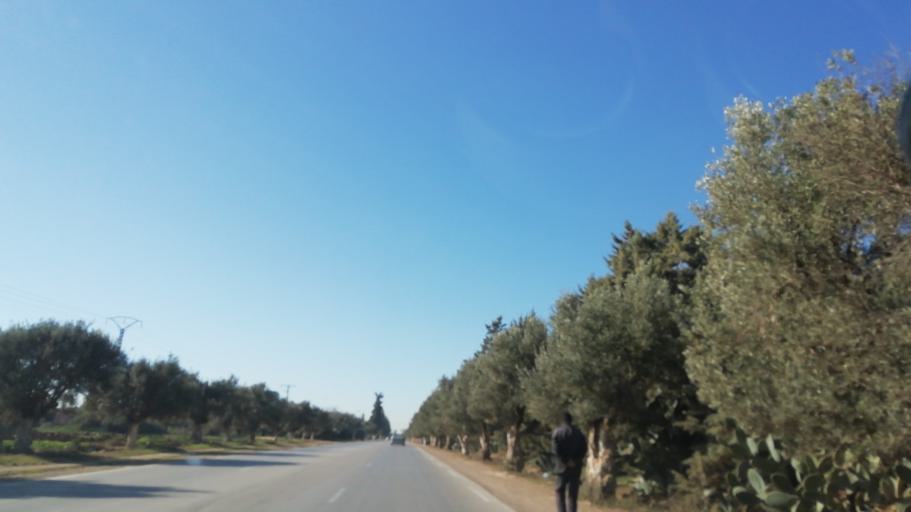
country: DZ
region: Tlemcen
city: Nedroma
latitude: 34.8322
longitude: -1.7870
